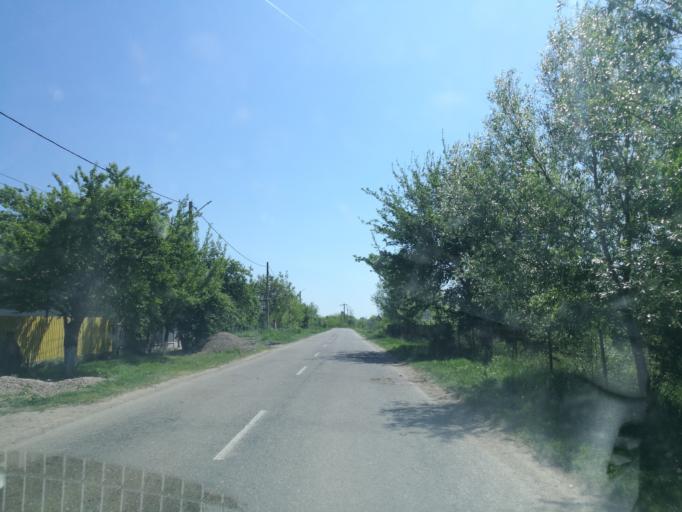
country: RO
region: Ialomita
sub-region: Comuna Adancata
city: Adancata
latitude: 44.7735
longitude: 26.4333
